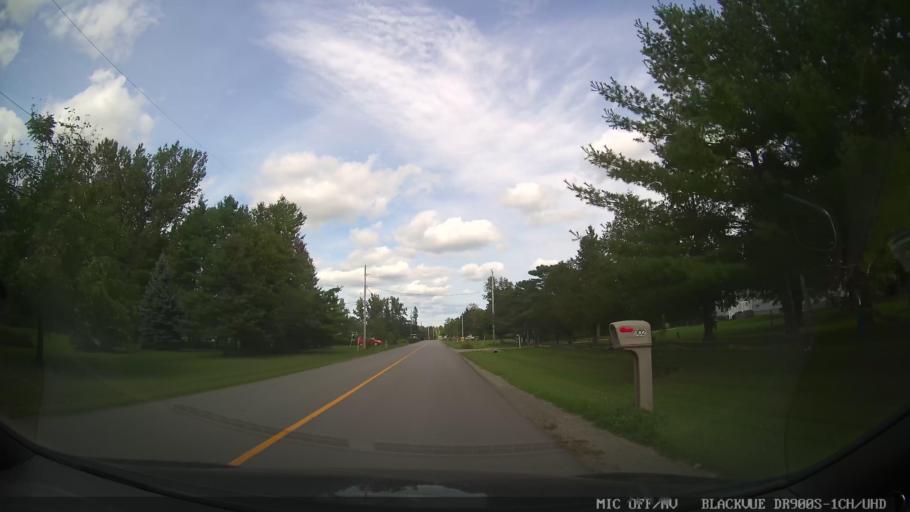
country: CA
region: Ontario
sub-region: Lanark County
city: Smiths Falls
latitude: 44.9311
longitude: -75.9518
